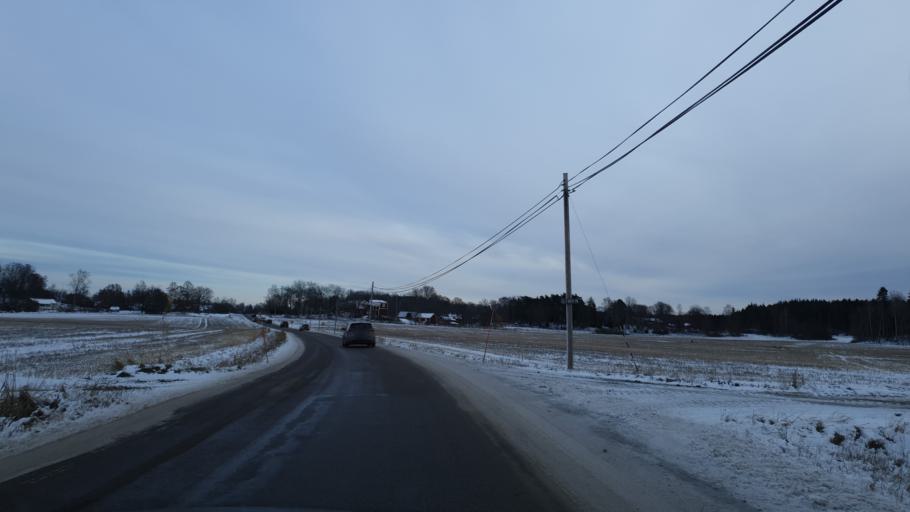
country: SE
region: Uppsala
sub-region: Habo Kommun
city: Balsta
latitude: 59.7078
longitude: 17.5819
